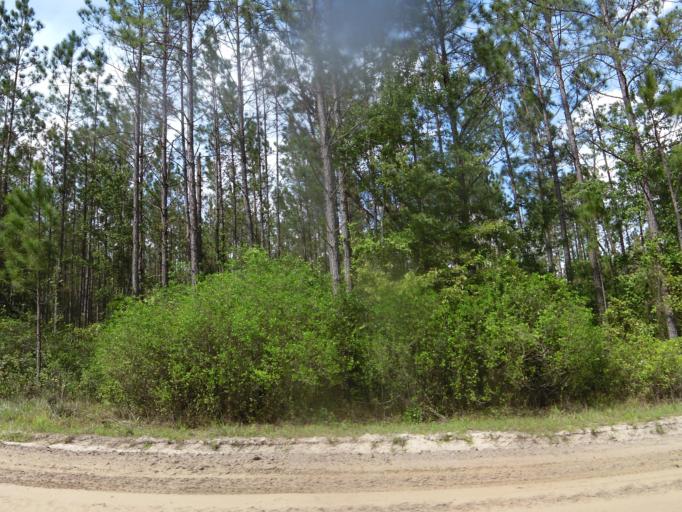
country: US
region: Georgia
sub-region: Charlton County
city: Folkston
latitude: 30.9403
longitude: -82.0102
